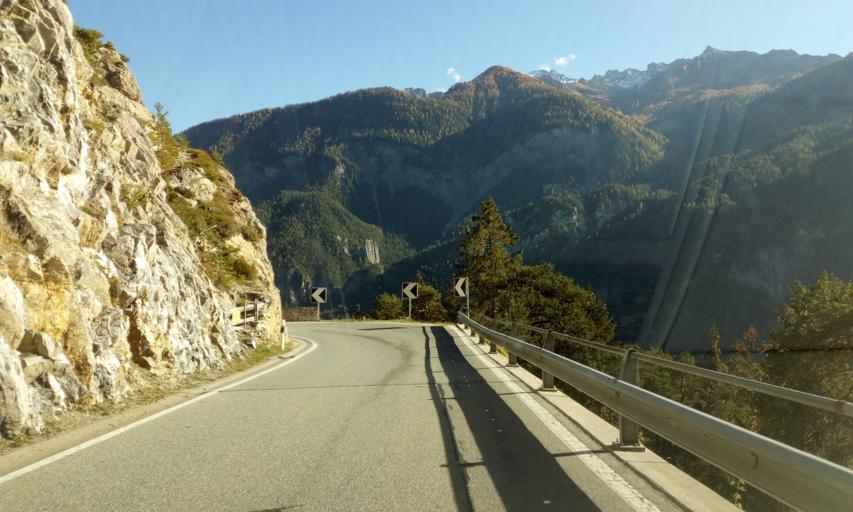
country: CH
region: Grisons
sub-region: Albula District
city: Tiefencastel
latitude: 46.6704
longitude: 9.6100
